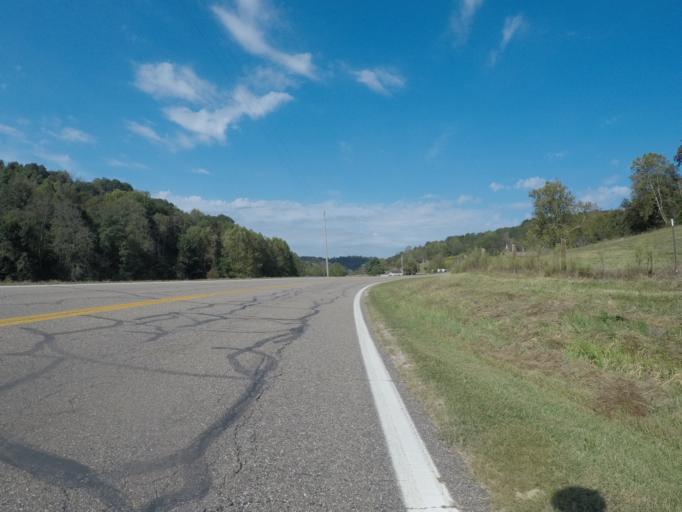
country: US
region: West Virginia
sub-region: Cabell County
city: Lesage
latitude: 38.6307
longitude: -82.4374
